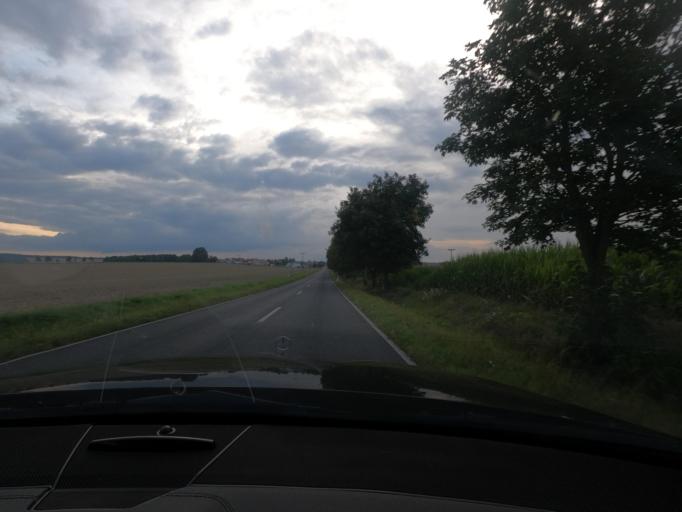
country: DE
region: Thuringia
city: Breitenworbis
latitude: 51.3987
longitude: 10.4188
